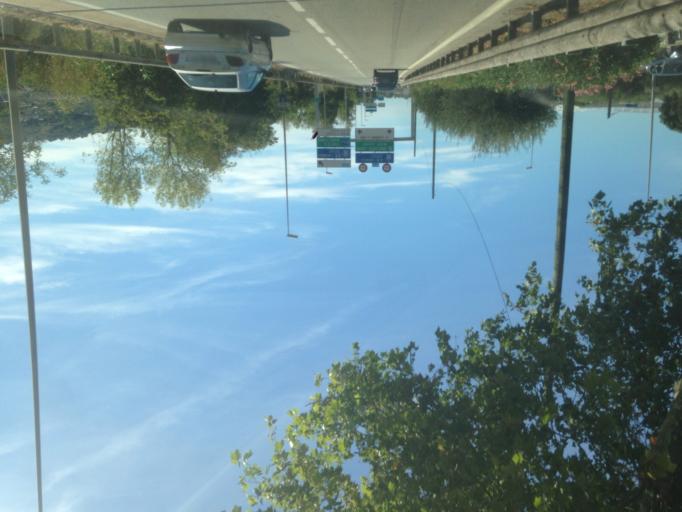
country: FR
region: Provence-Alpes-Cote d'Azur
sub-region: Departement des Alpes-Maritimes
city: La Gaude
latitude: 43.7134
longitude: 7.1872
